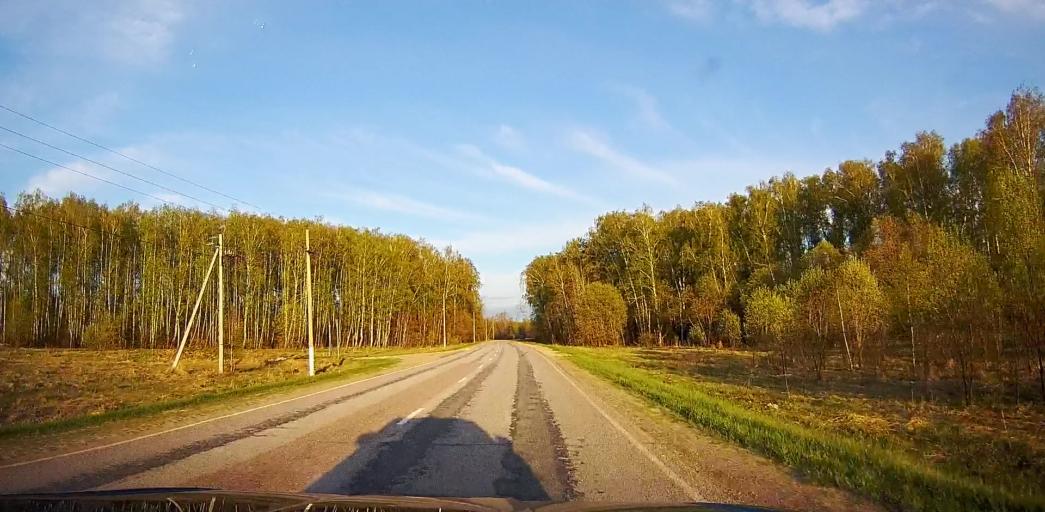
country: RU
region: Moskovskaya
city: Meshcherino
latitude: 55.2285
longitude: 38.3835
